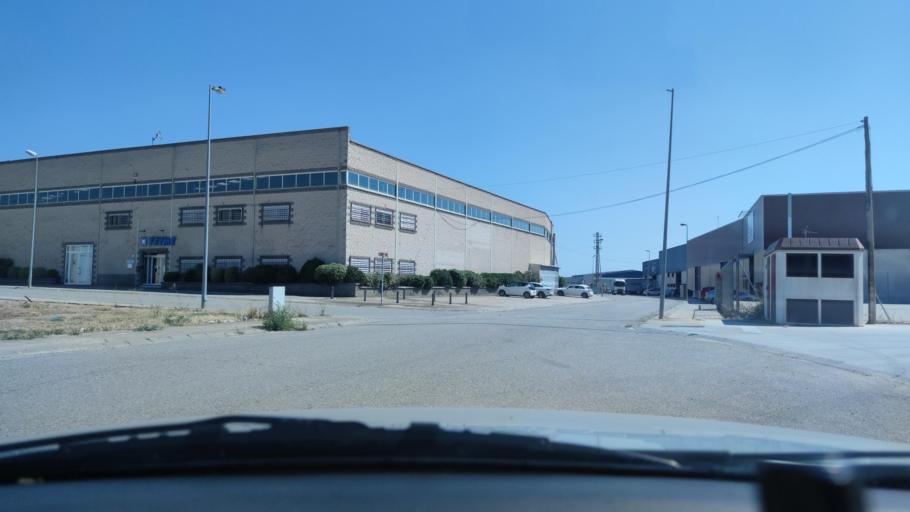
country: ES
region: Catalonia
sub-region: Provincia de Lleida
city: Torrefarrera
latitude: 41.6796
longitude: 0.6293
